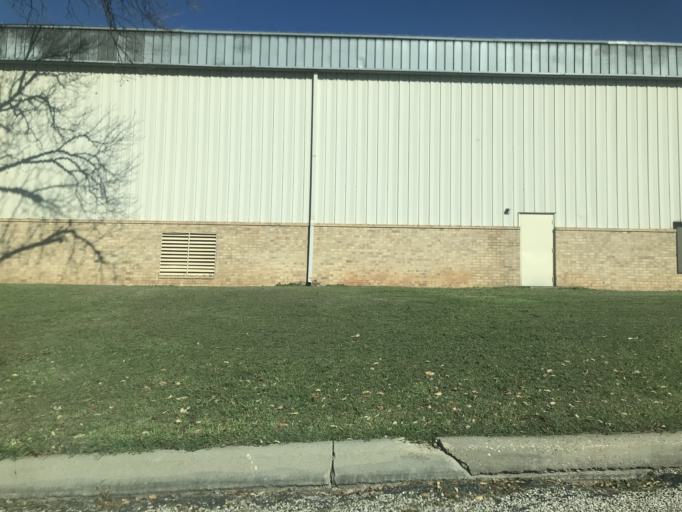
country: US
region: Texas
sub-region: Tom Green County
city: San Angelo
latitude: 31.4532
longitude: -100.4459
